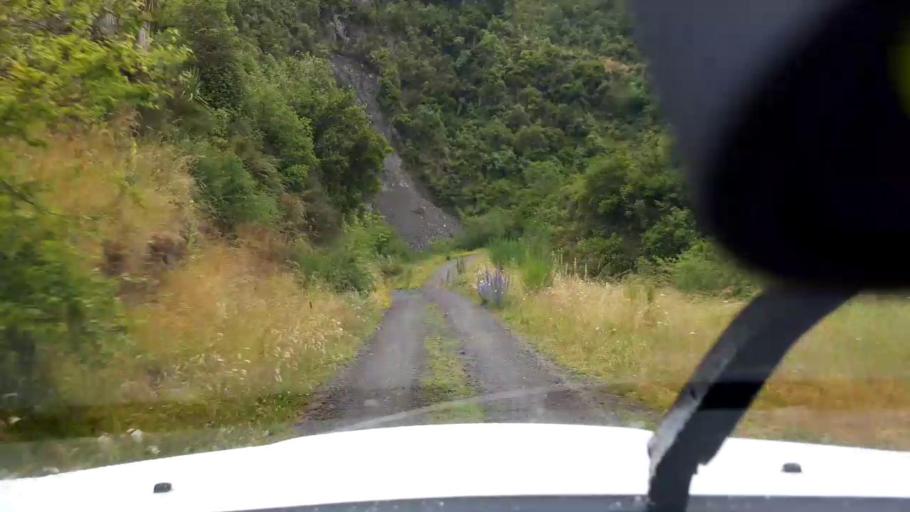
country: NZ
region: Canterbury
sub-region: Timaru District
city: Pleasant Point
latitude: -44.0445
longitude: 171.0186
